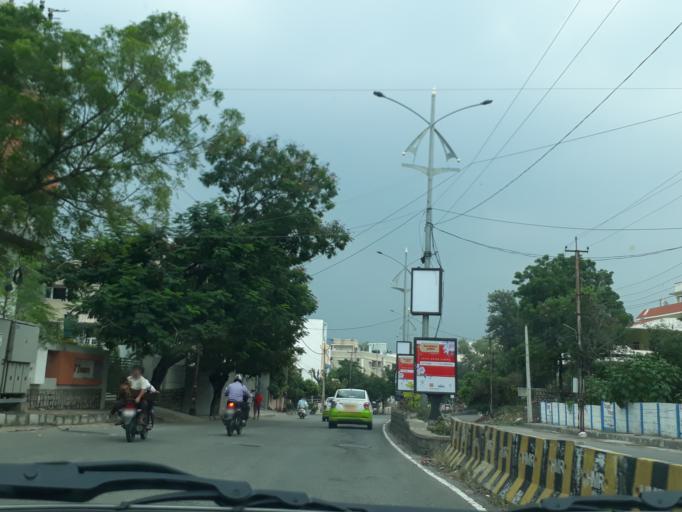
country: IN
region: Telangana
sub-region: Rangareddi
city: Kukatpalli
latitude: 17.4345
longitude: 78.4153
